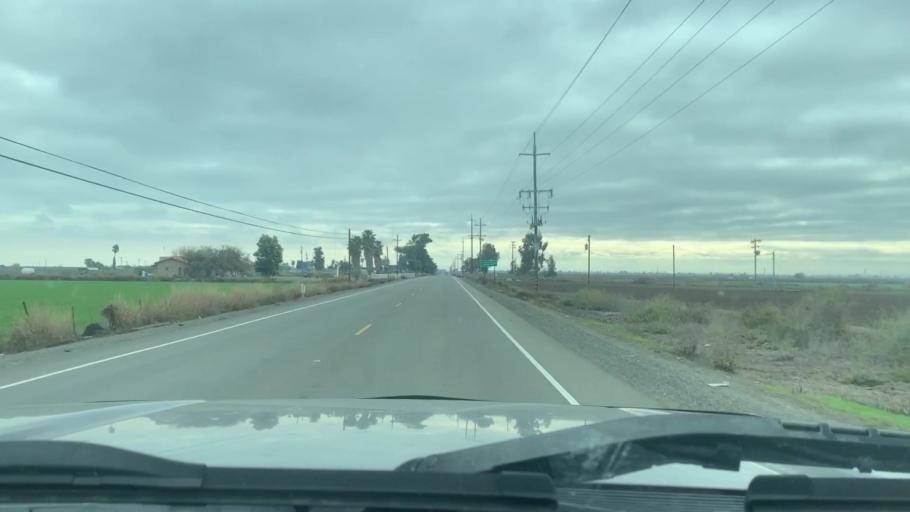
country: US
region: California
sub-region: Merced County
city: Los Banos
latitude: 37.1068
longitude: -120.8349
